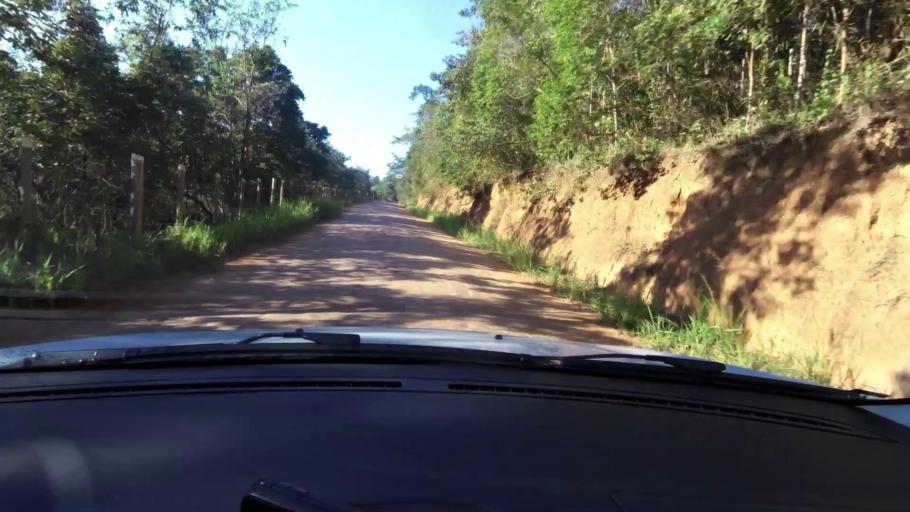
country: BR
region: Espirito Santo
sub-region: Guarapari
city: Guarapari
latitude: -20.7270
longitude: -40.5891
